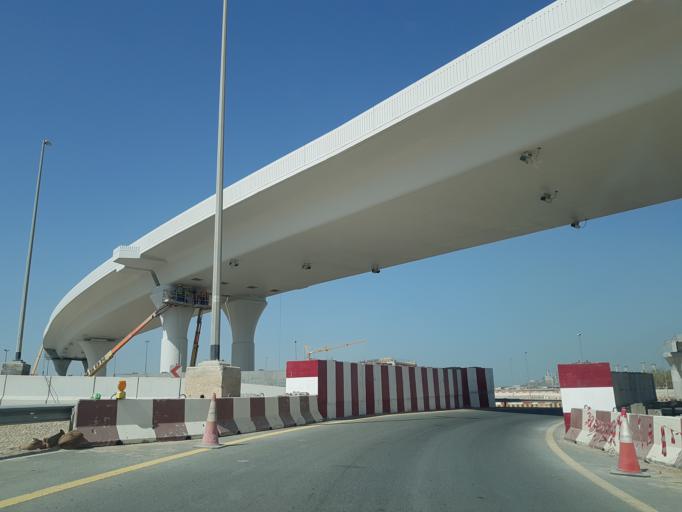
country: AE
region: Dubai
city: Dubai
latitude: 25.0130
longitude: 55.0935
